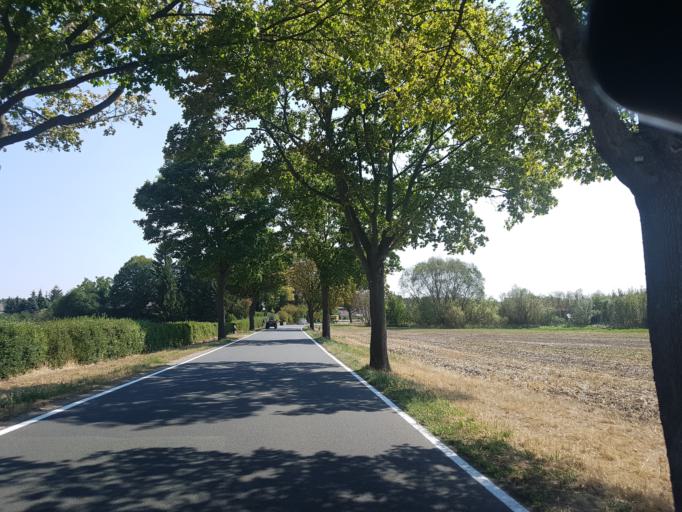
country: DE
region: Brandenburg
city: Wiesenburg
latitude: 52.0607
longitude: 12.3844
